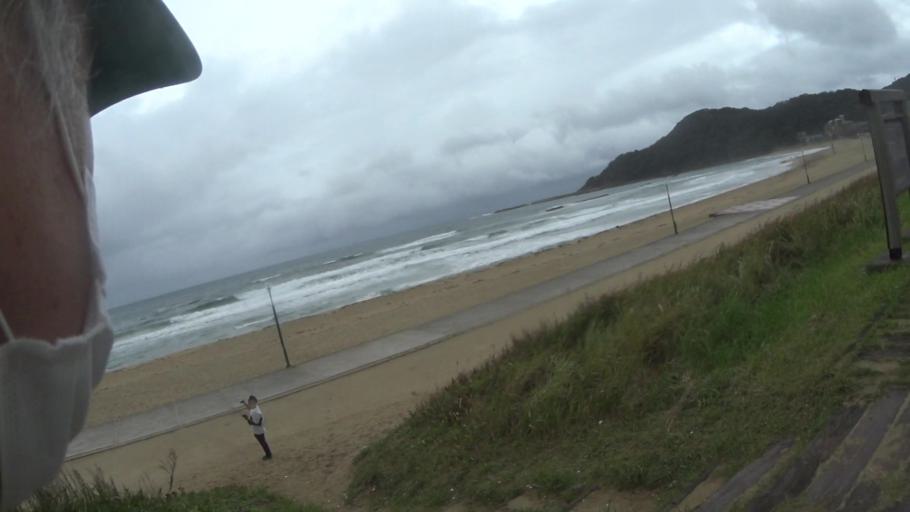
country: JP
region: Hyogo
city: Toyooka
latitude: 35.6617
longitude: 134.9636
